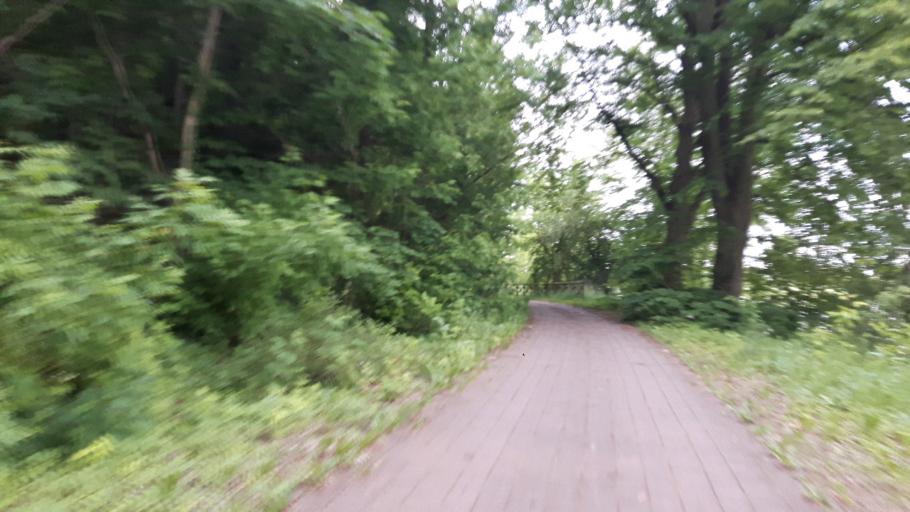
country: DE
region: Brandenburg
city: Gartz
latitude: 53.2242
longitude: 14.4086
